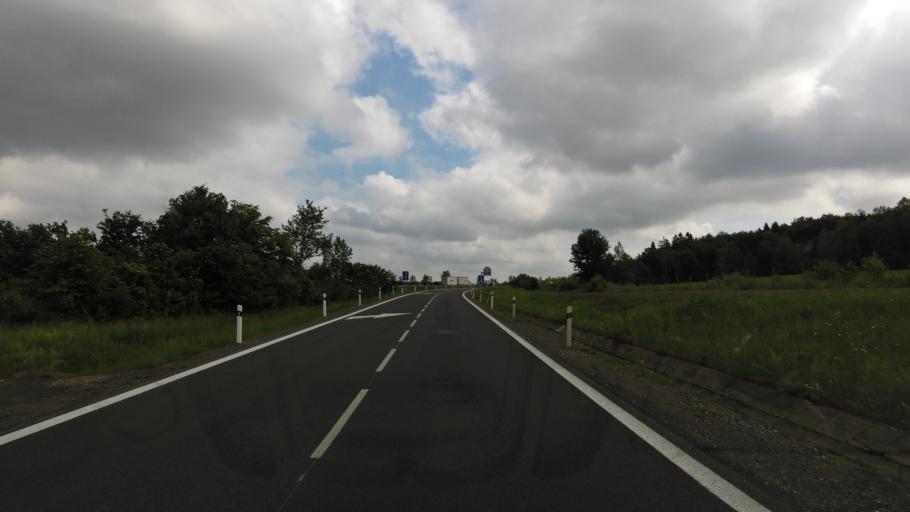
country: CZ
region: Plzensky
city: Dysina
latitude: 49.7362
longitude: 13.5132
